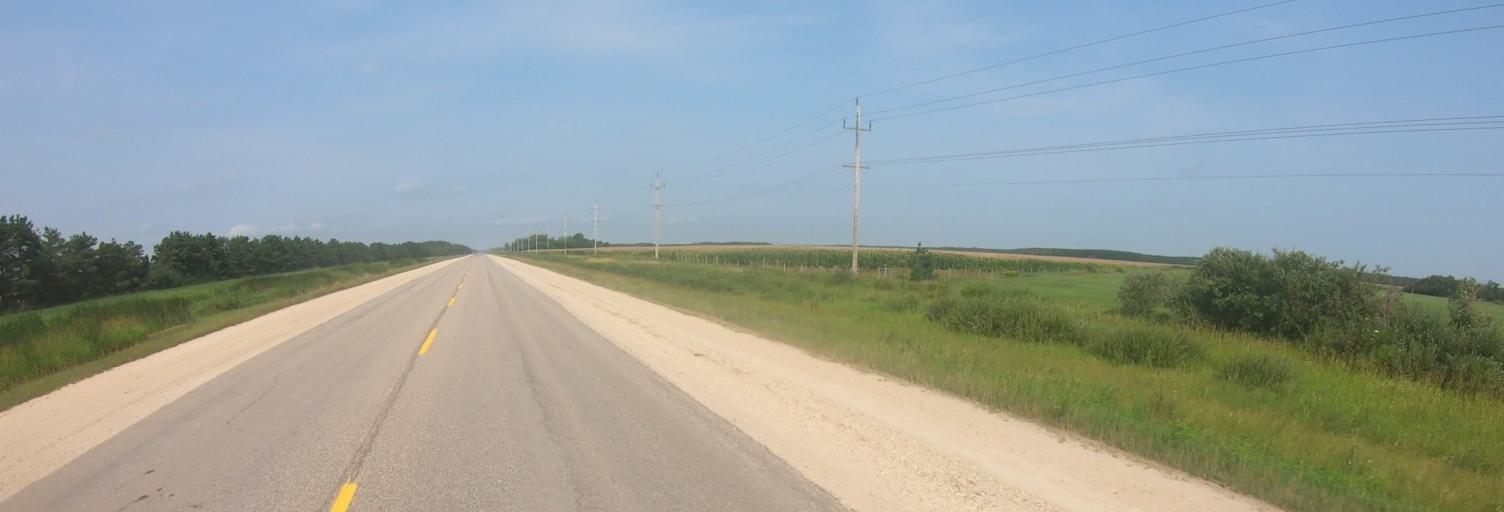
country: CA
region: Manitoba
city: La Broquerie
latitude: 49.3214
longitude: -96.5894
